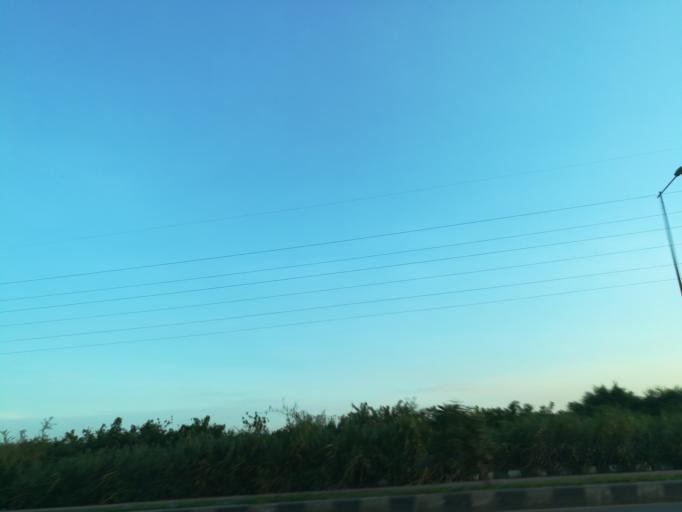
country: NG
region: Lagos
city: Ebute Ikorodu
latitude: 6.6215
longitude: 3.4528
